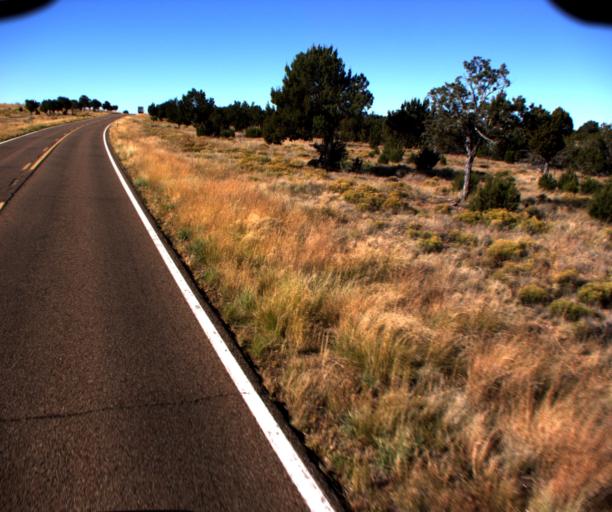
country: US
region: Arizona
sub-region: Navajo County
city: Heber-Overgaard
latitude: 34.4734
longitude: -110.4689
